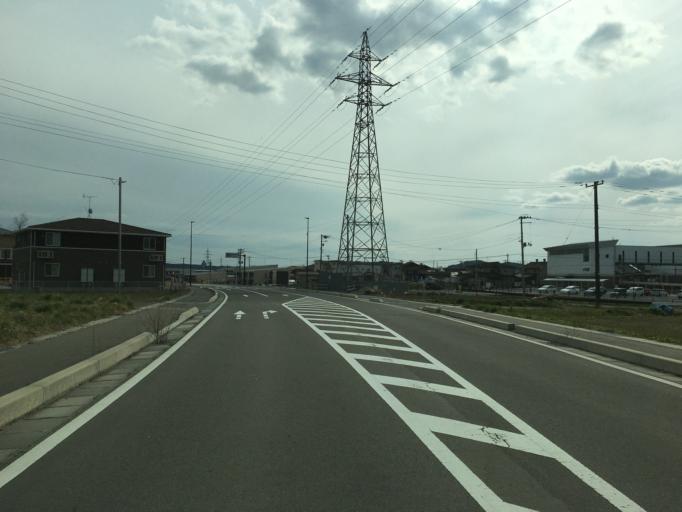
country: JP
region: Fukushima
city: Nihommatsu
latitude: 37.6132
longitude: 140.4683
